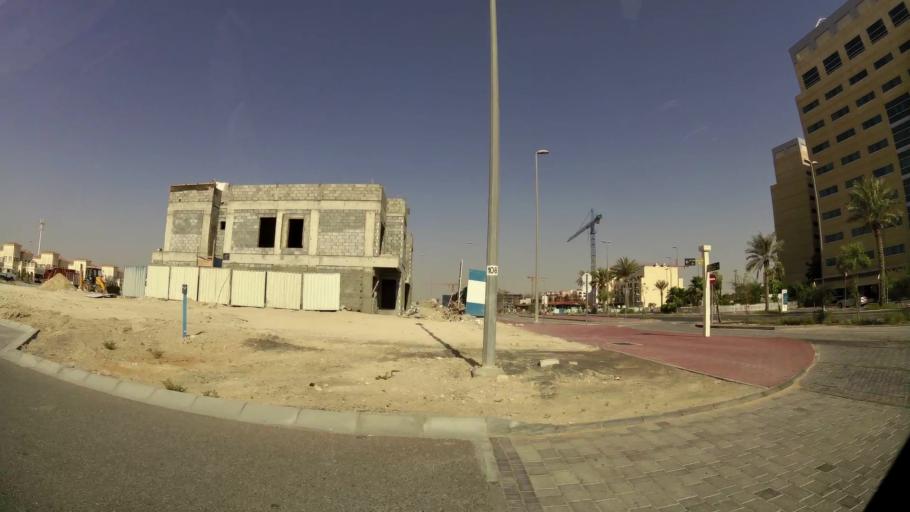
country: AE
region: Dubai
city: Dubai
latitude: 25.0686
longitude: 55.2094
